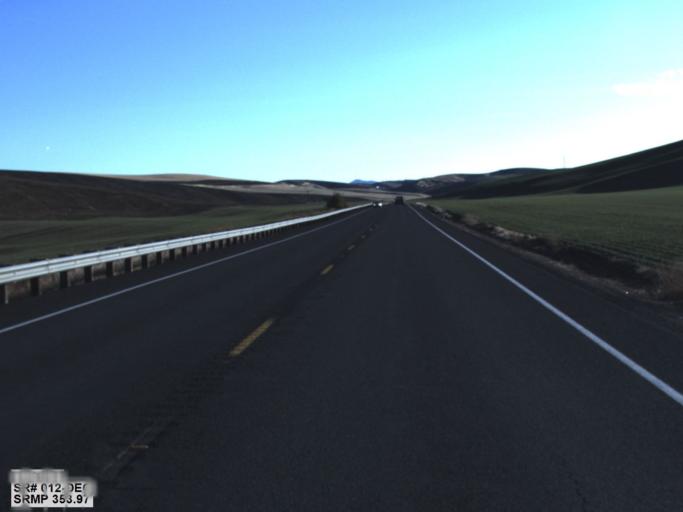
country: US
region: Washington
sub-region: Walla Walla County
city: Waitsburg
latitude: 46.2198
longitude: -118.1376
